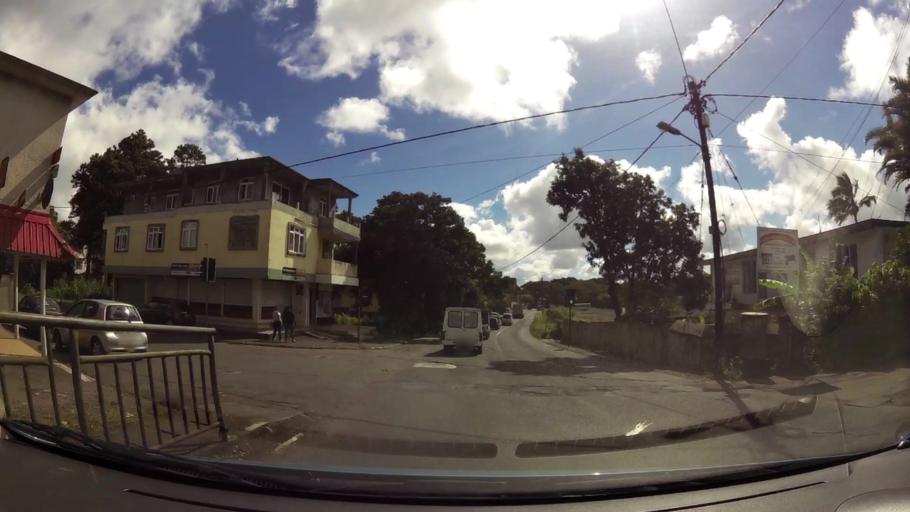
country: MU
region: Plaines Wilhems
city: Curepipe
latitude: -20.3309
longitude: 57.5324
